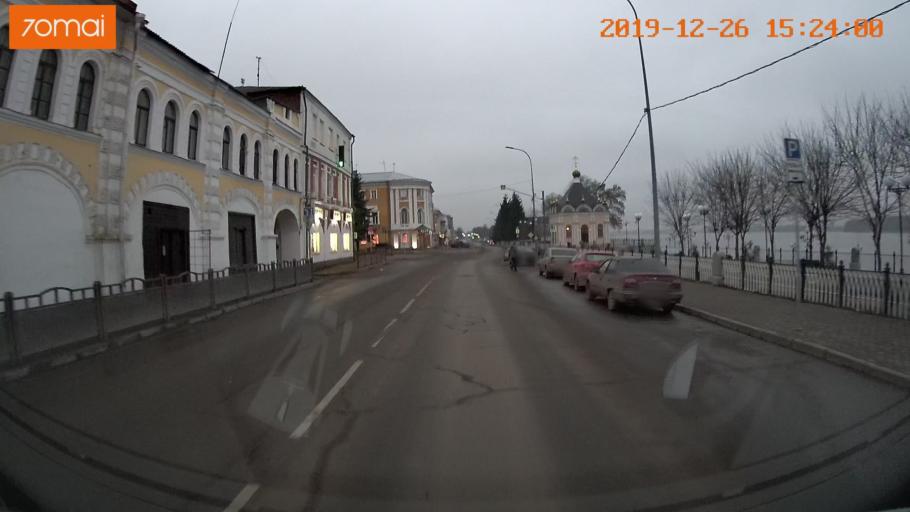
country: RU
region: Jaroslavl
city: Rybinsk
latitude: 58.0498
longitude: 38.8539
